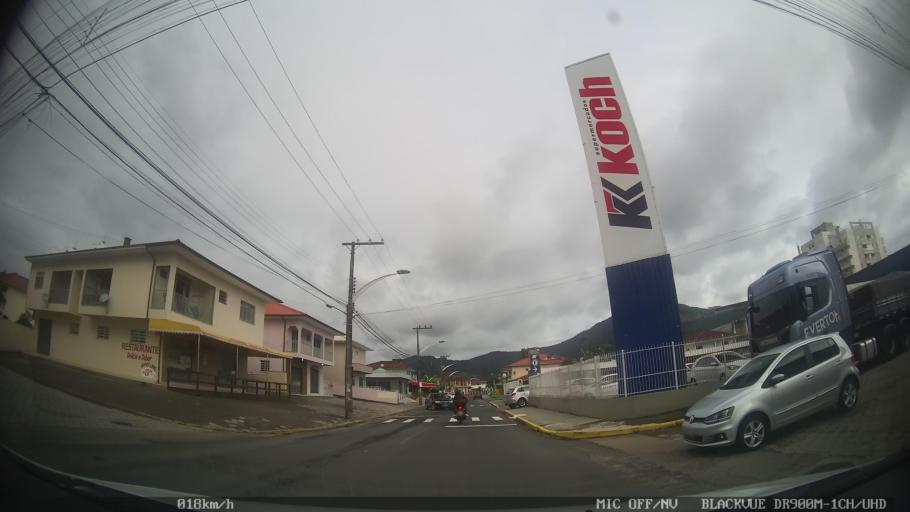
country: BR
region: Santa Catarina
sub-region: Biguacu
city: Biguacu
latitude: -27.5076
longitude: -48.6513
